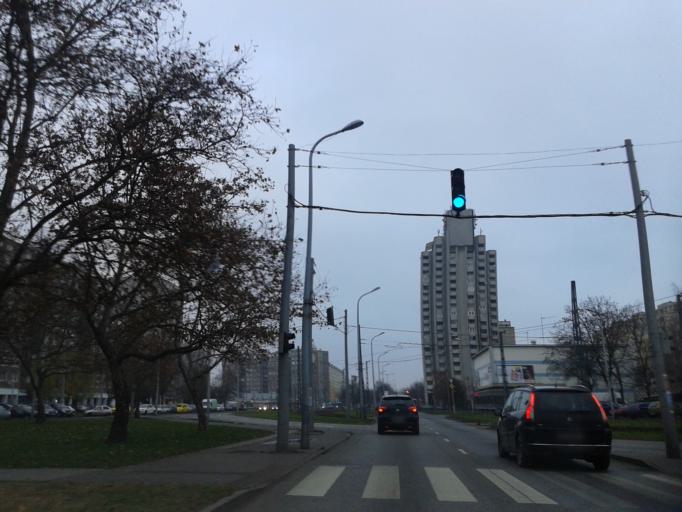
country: HU
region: Budapest
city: Budapest XV. keruelet
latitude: 47.5423
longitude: 19.1401
